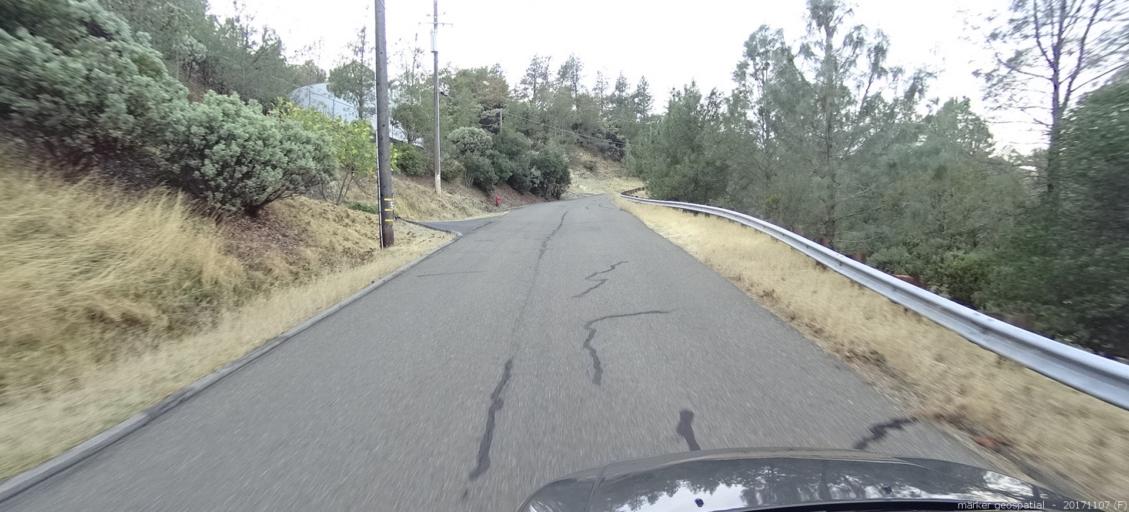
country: US
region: California
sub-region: Shasta County
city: Shasta
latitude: 40.5399
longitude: -122.4946
